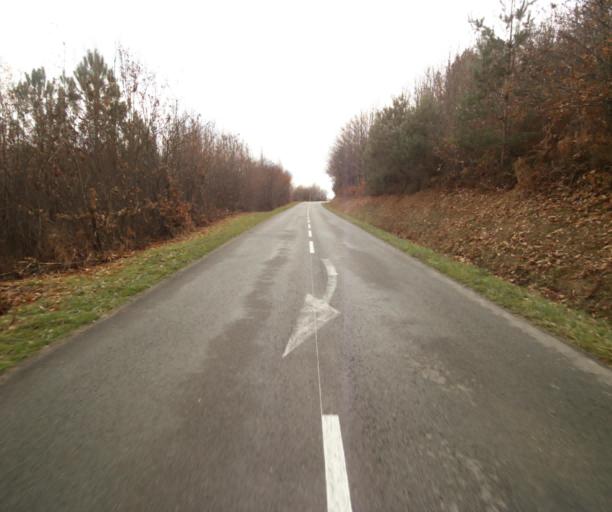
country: FR
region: Limousin
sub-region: Departement de la Correze
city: Chameyrat
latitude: 45.2616
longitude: 1.7057
